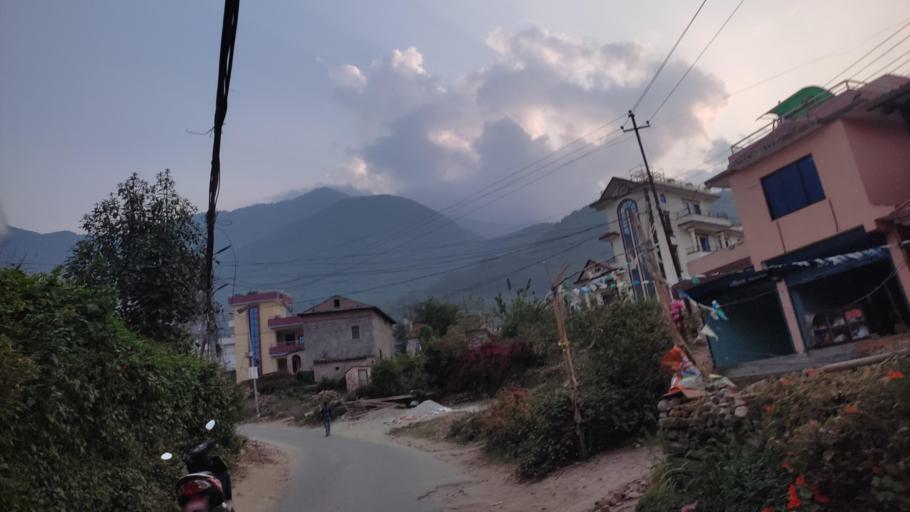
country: NP
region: Central Region
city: Kirtipur
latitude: 27.6647
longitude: 85.2537
